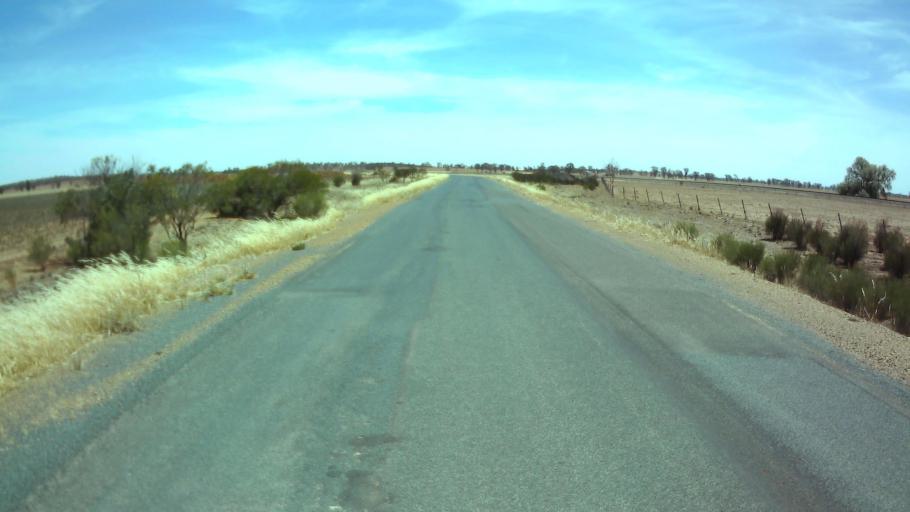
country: AU
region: New South Wales
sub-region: Weddin
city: Grenfell
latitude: -33.7530
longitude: 147.7653
